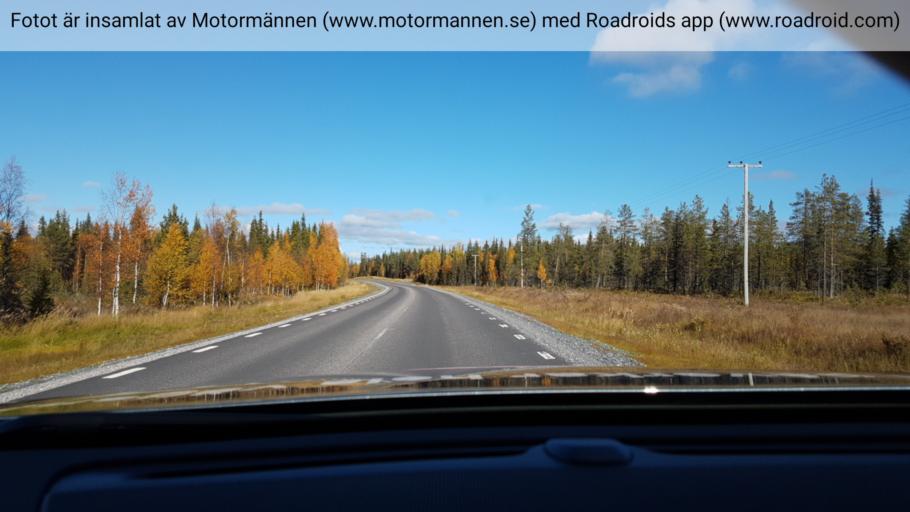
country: SE
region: Norrbotten
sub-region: Gallivare Kommun
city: Gaellivare
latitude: 67.0426
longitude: 20.7360
